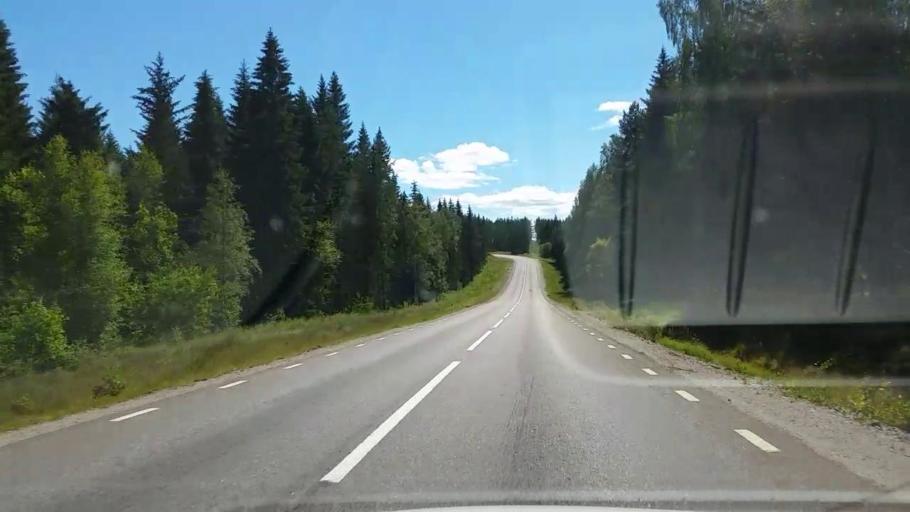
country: SE
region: Gaevleborg
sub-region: Ovanakers Kommun
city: Edsbyn
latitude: 61.0800
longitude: 15.8016
